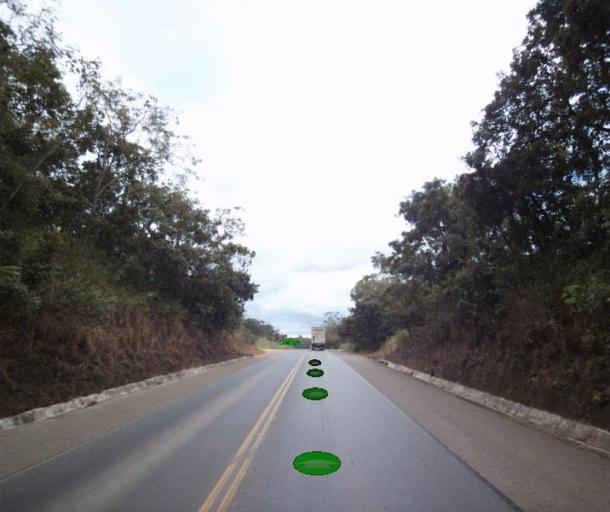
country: BR
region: Goias
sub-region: Itapaci
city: Itapaci
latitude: -14.8147
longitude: -49.2939
